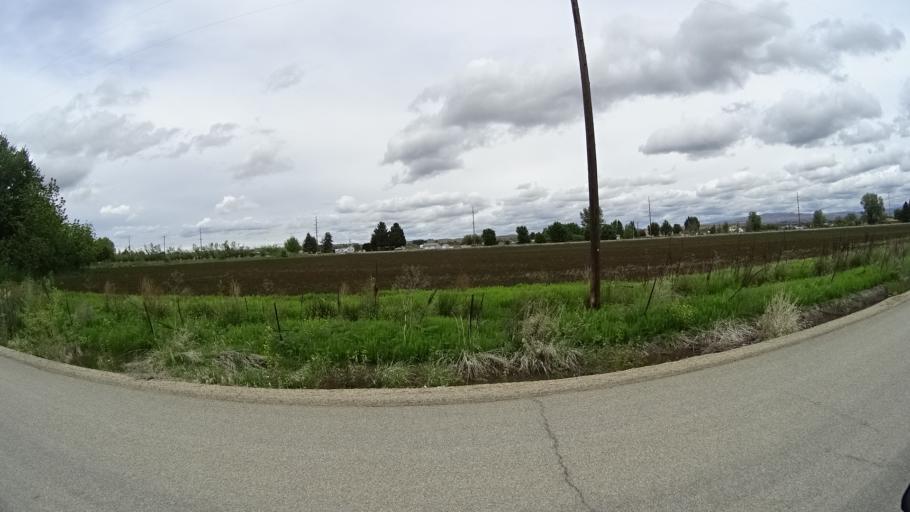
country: US
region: Idaho
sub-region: Ada County
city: Star
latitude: 43.6891
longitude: -116.4375
